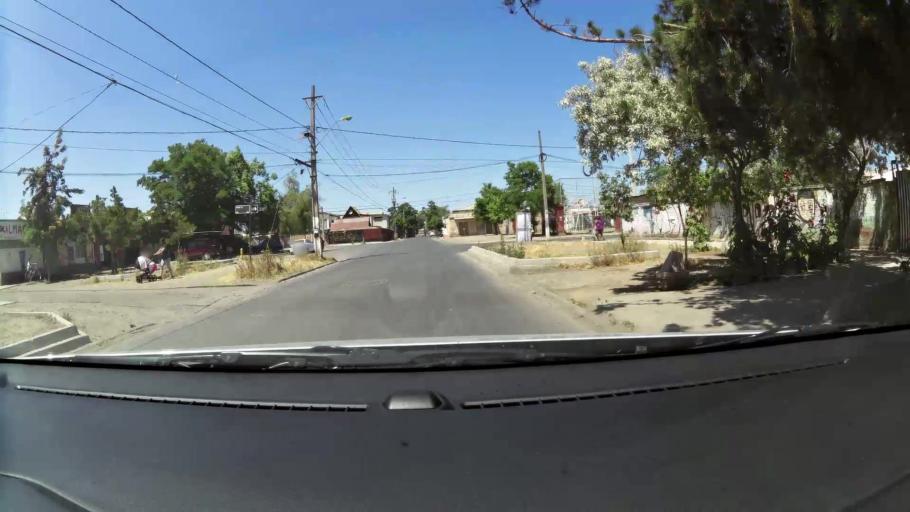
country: CL
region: Santiago Metropolitan
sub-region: Provincia de Santiago
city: La Pintana
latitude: -33.5654
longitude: -70.6630
